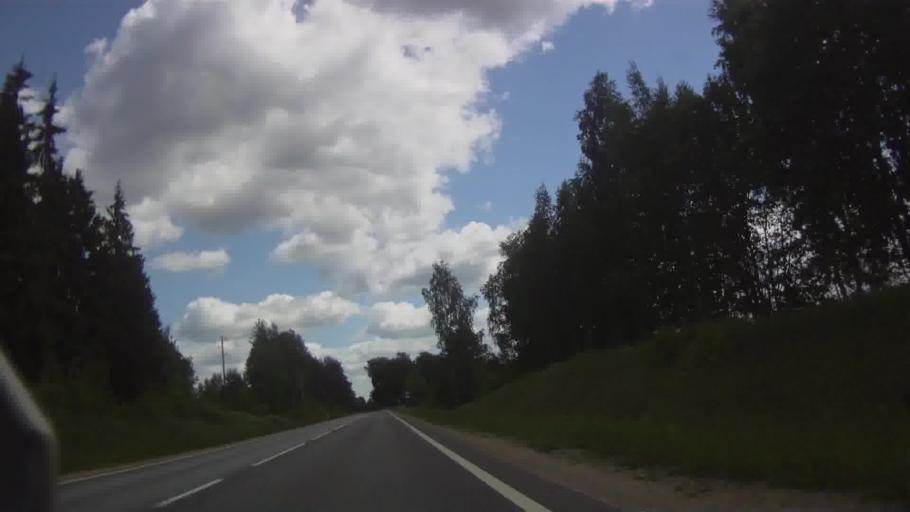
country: LV
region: Jekabpils Rajons
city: Jekabpils
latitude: 56.5330
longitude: 26.0268
